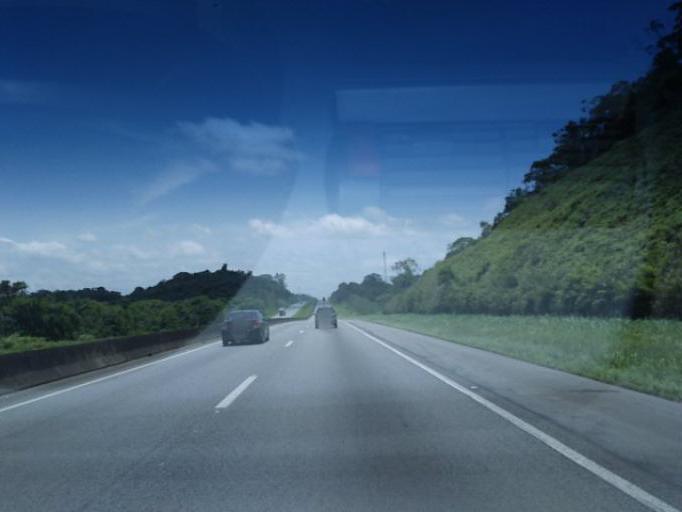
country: BR
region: Sao Paulo
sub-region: Registro
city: Registro
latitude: -24.4368
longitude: -47.7935
